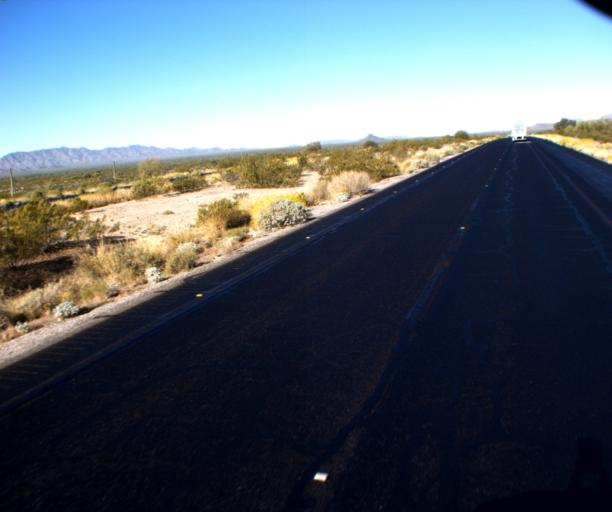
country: US
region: Arizona
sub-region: Pinal County
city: Maricopa
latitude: 32.8384
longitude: -112.2225
